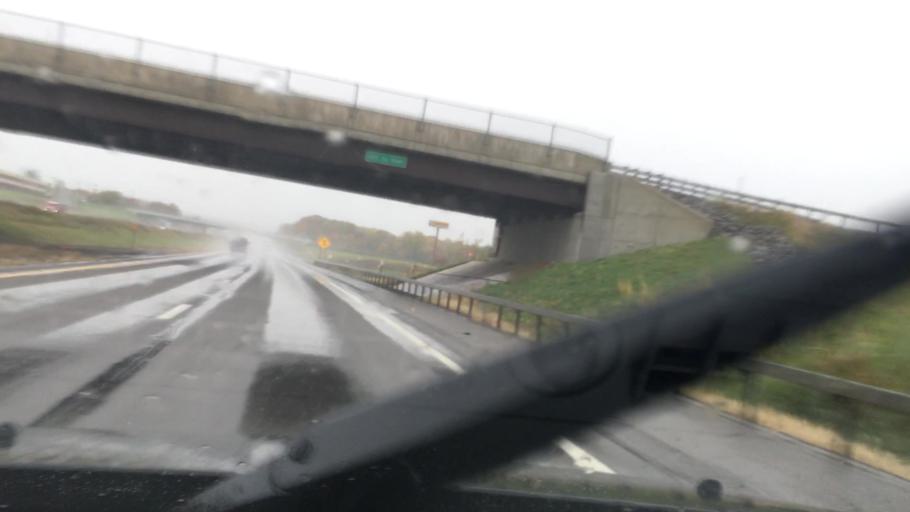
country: US
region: New York
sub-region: Erie County
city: Blasdell
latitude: 42.7940
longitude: -78.8170
